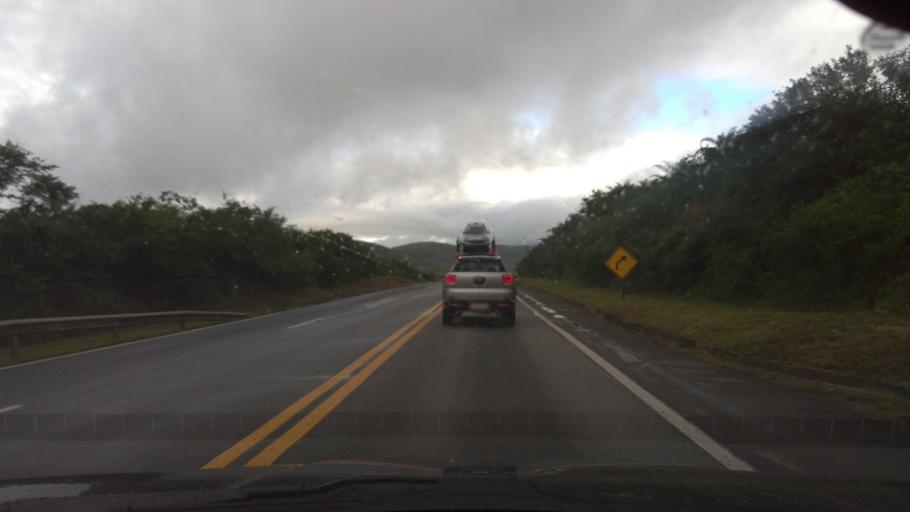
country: BR
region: Bahia
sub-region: Santa Ines
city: Santa Ines
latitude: -13.2521
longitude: -40.0133
